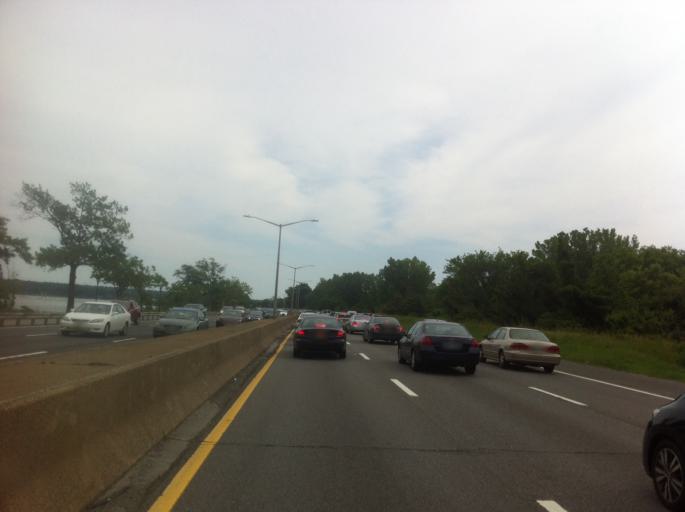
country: US
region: New York
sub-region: Nassau County
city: East Atlantic Beach
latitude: 40.7846
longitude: -73.7736
